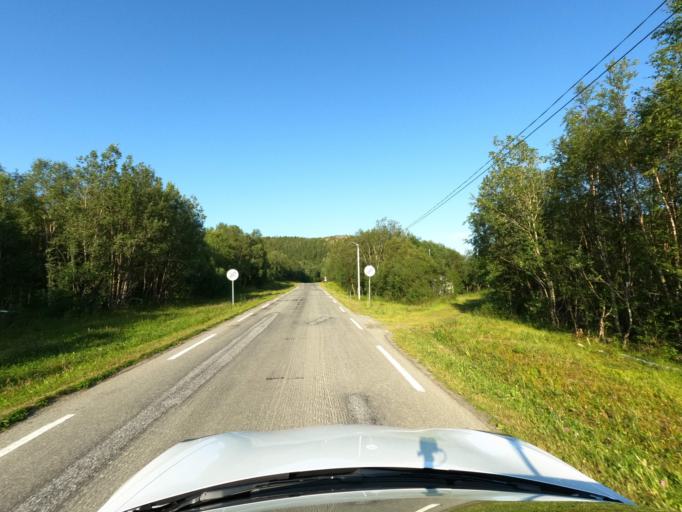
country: NO
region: Nordland
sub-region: Narvik
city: Bjerkvik
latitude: 68.5527
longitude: 17.5666
